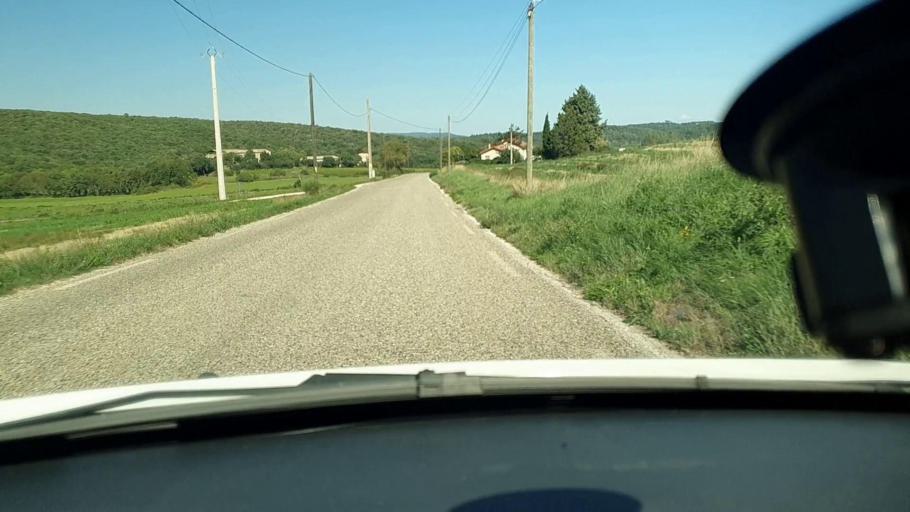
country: FR
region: Languedoc-Roussillon
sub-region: Departement du Gard
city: Goudargues
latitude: 44.1466
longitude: 4.4486
